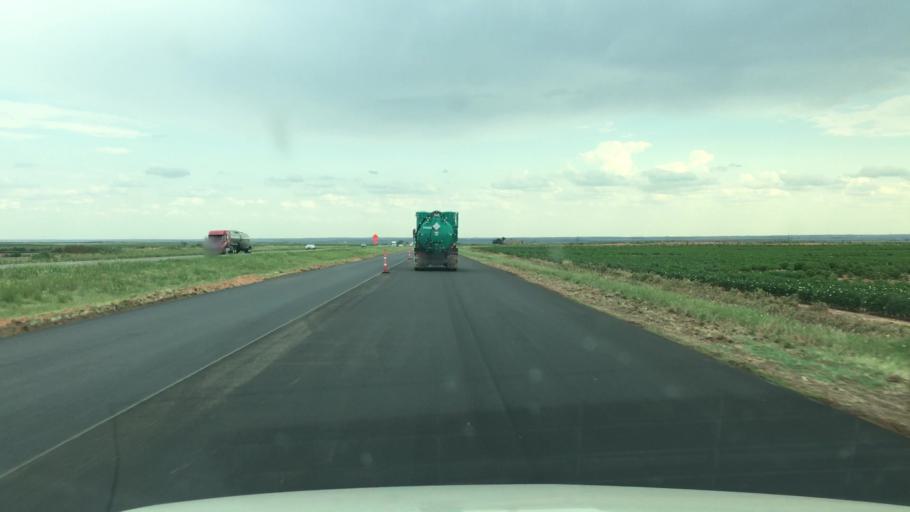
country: US
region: Texas
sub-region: Hall County
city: Memphis
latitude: 34.6264
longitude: -100.4745
